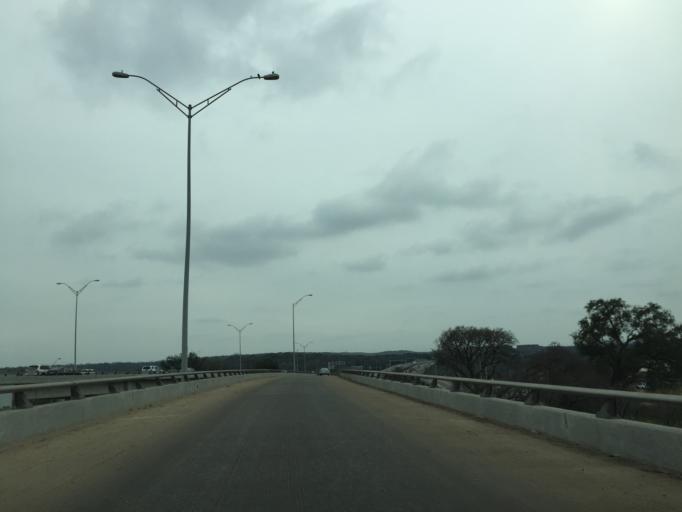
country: US
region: Texas
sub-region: Travis County
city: Rollingwood
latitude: 30.2785
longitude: -97.7690
